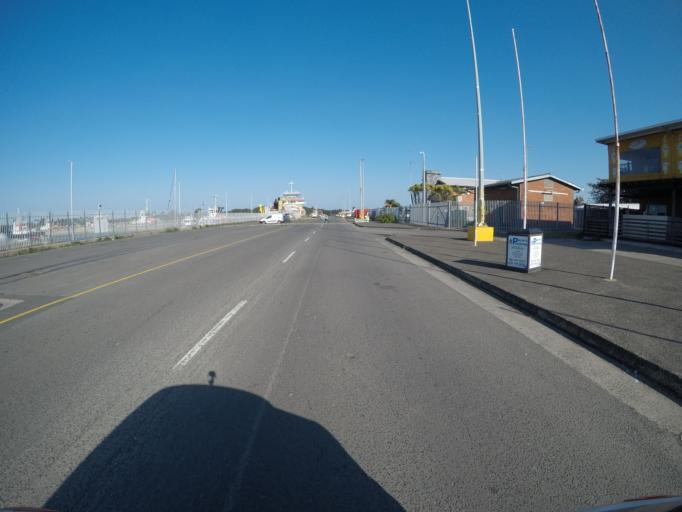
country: ZA
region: KwaZulu-Natal
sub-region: uThungulu District Municipality
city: Richards Bay
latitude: -28.7943
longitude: 32.0779
